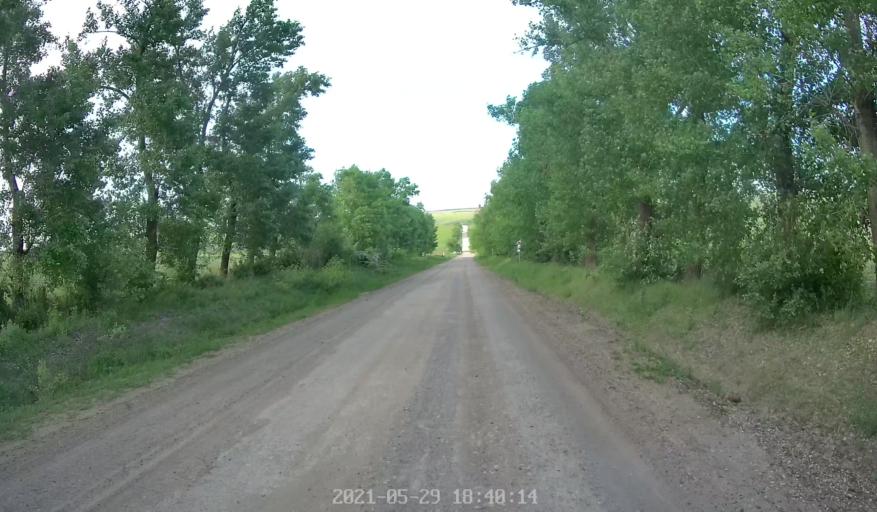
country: MD
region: Chisinau
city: Singera
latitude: 46.8040
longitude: 28.9502
